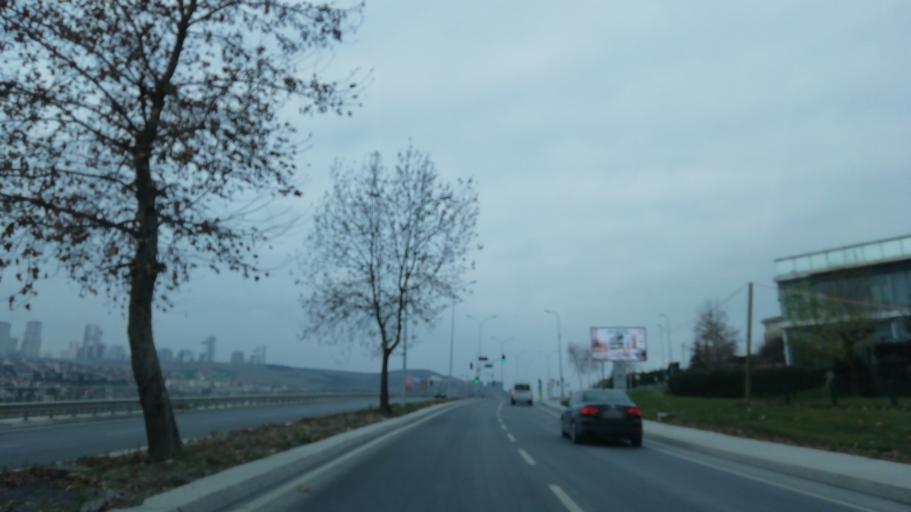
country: TR
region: Istanbul
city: Esenyurt
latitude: 41.0848
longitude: 28.6792
